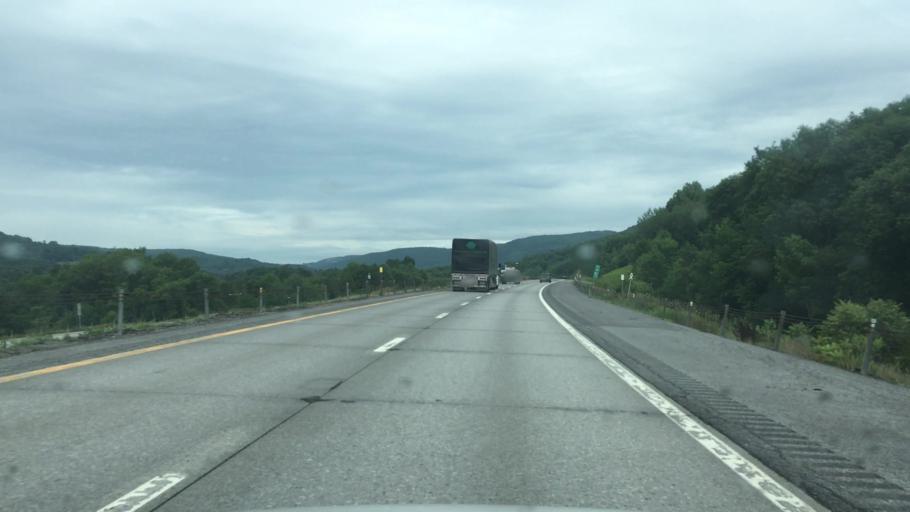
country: US
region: New York
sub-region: Otsego County
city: Worcester
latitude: 42.5858
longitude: -74.7528
